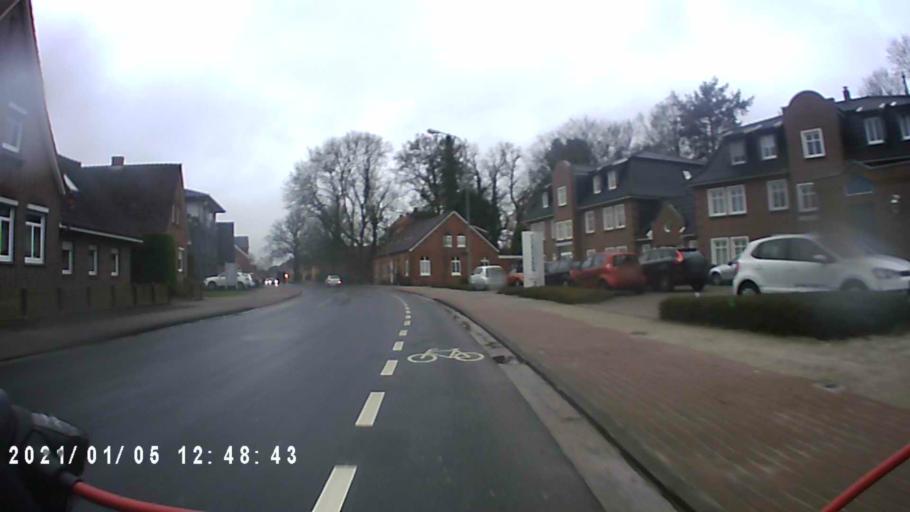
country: DE
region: Lower Saxony
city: Leer
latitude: 53.2389
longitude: 7.4981
